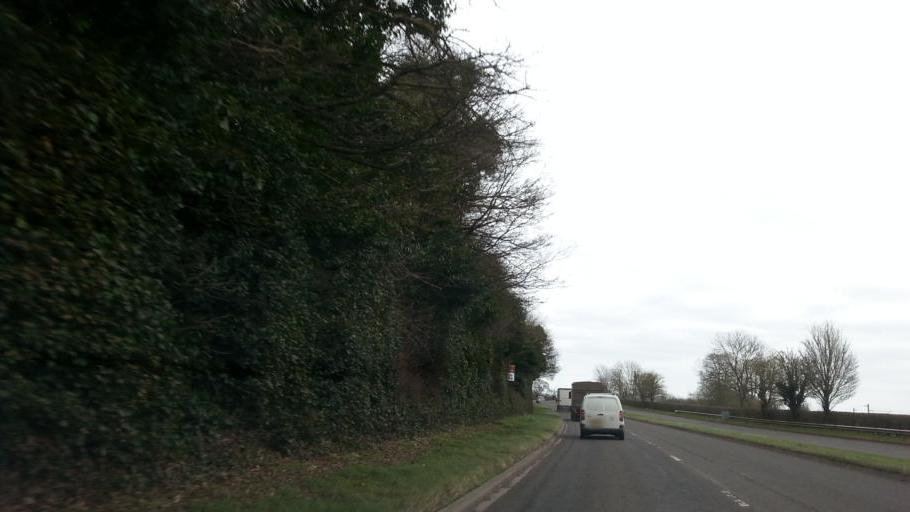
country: GB
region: England
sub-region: Staffordshire
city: Stafford
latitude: 52.8499
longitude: -2.0558
